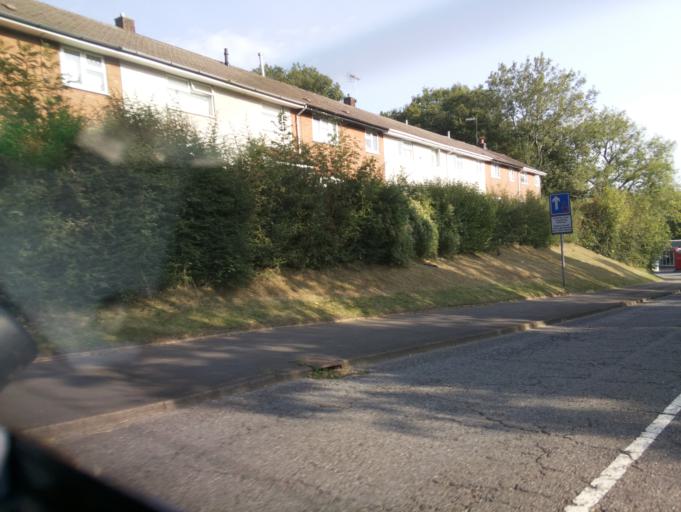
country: GB
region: Wales
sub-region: Torfaen County Borough
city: Cwmbran
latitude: 51.6599
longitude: -3.0364
